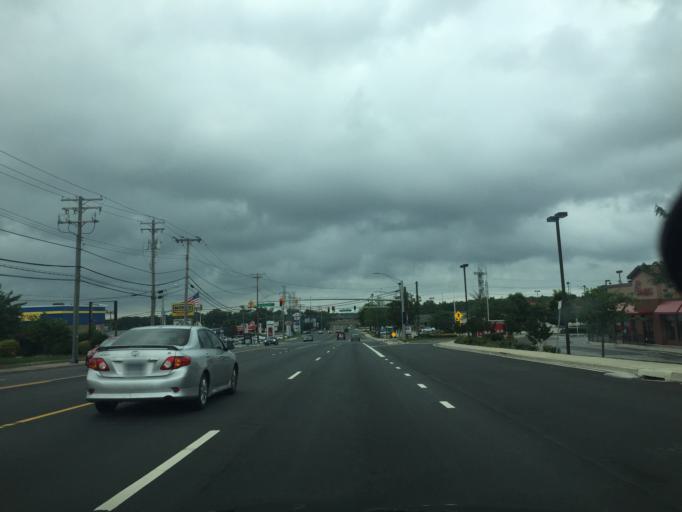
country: US
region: Maryland
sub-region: Baltimore County
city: Rosedale
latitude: 39.2952
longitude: -76.5106
